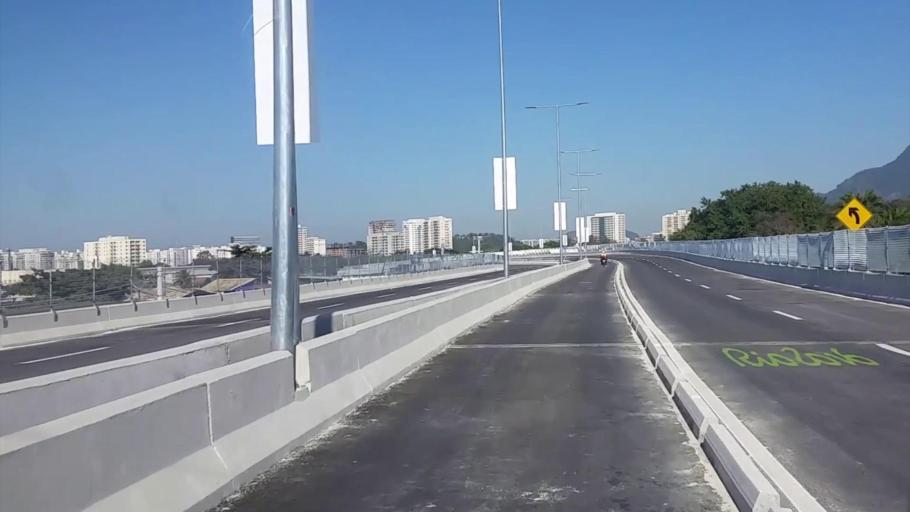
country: BR
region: Rio de Janeiro
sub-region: Nilopolis
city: Nilopolis
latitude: -22.9549
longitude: -43.3921
